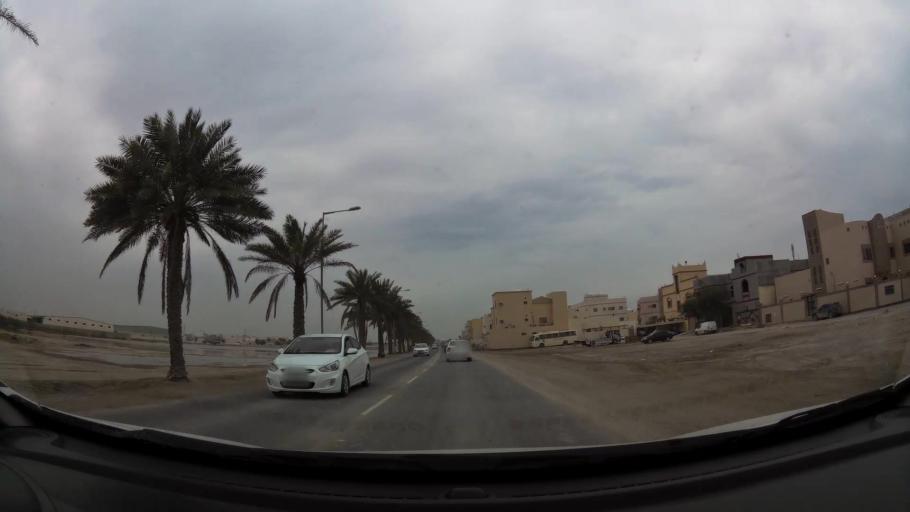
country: BH
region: Northern
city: Sitrah
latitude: 26.1678
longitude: 50.6219
